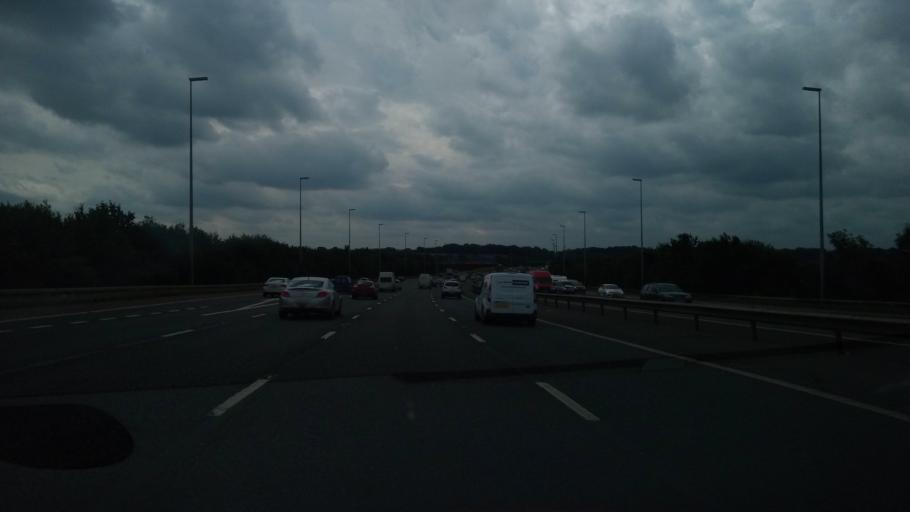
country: GB
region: England
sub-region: Lancashire
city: Goosnargh
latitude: 53.7718
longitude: -2.6388
